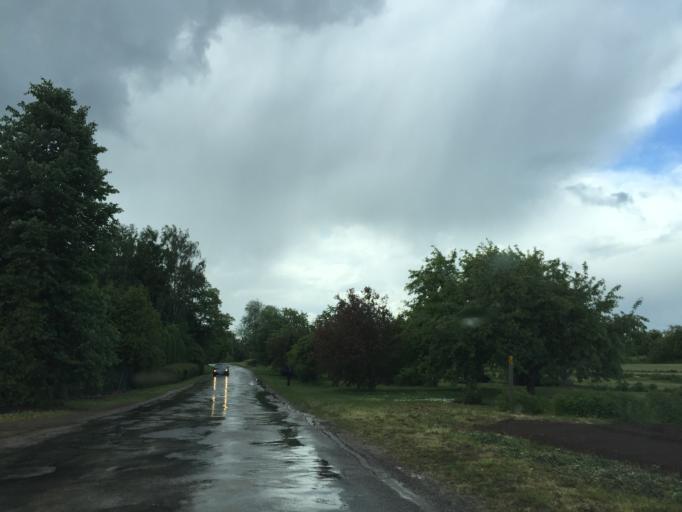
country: LV
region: Lecava
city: Iecava
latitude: 56.5964
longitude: 24.1880
